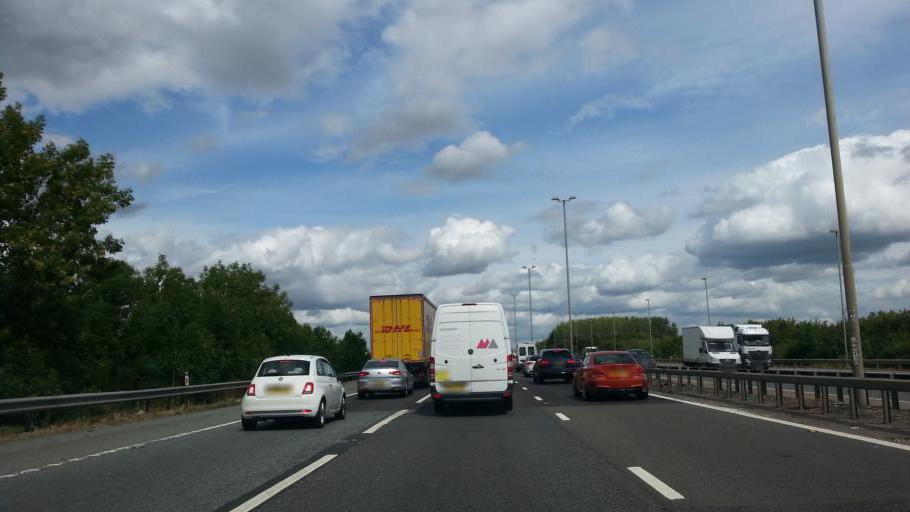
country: GB
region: England
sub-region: Essex
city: Little Hallingbury
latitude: 51.8588
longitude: 0.1881
